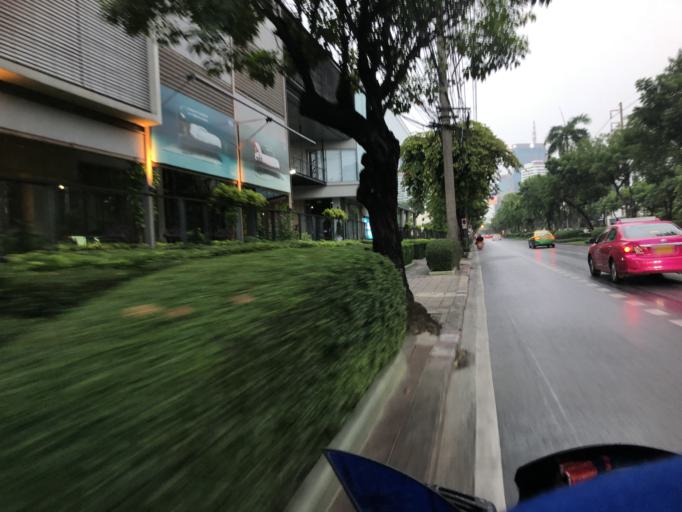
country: TH
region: Bangkok
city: Khlong Toei
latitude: 13.7136
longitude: 100.5798
